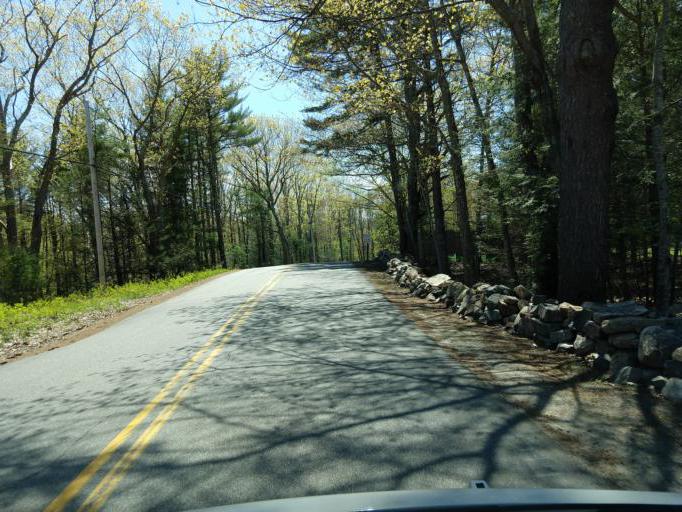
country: US
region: Maine
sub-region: York County
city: Cape Neddick
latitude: 43.2259
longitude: -70.6288
